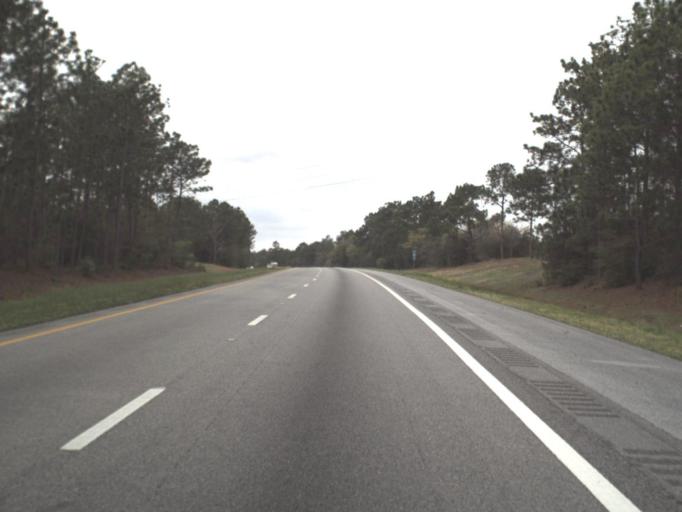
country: US
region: Florida
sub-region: Okaloosa County
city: Crestview
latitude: 30.7259
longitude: -86.4889
